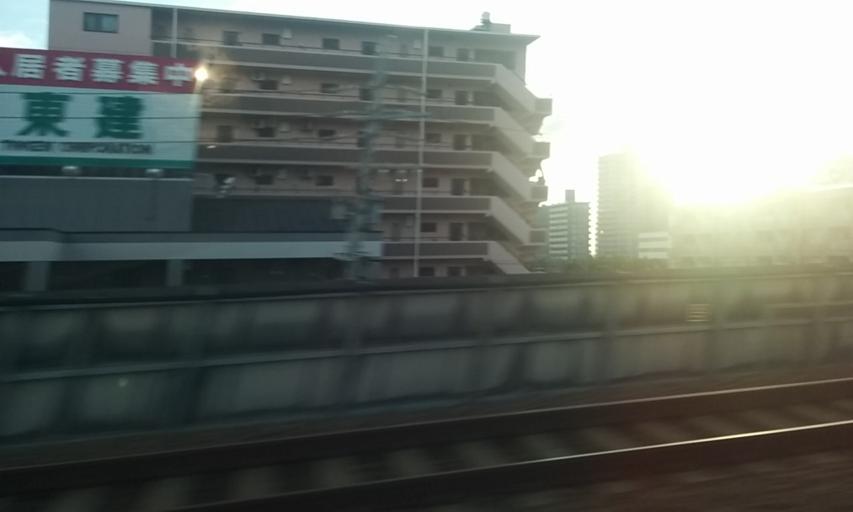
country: JP
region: Aichi
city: Anjo
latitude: 34.9660
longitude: 137.0632
